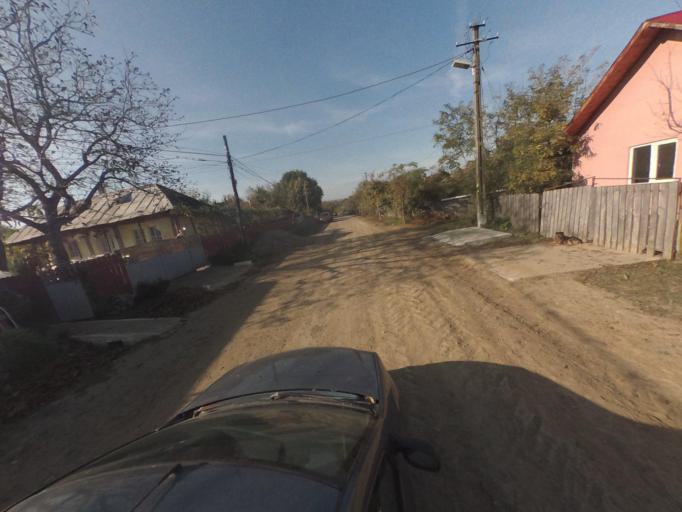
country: RO
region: Vaslui
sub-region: Comuna Bacesti
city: Bacesti
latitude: 46.8710
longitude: 27.2001
